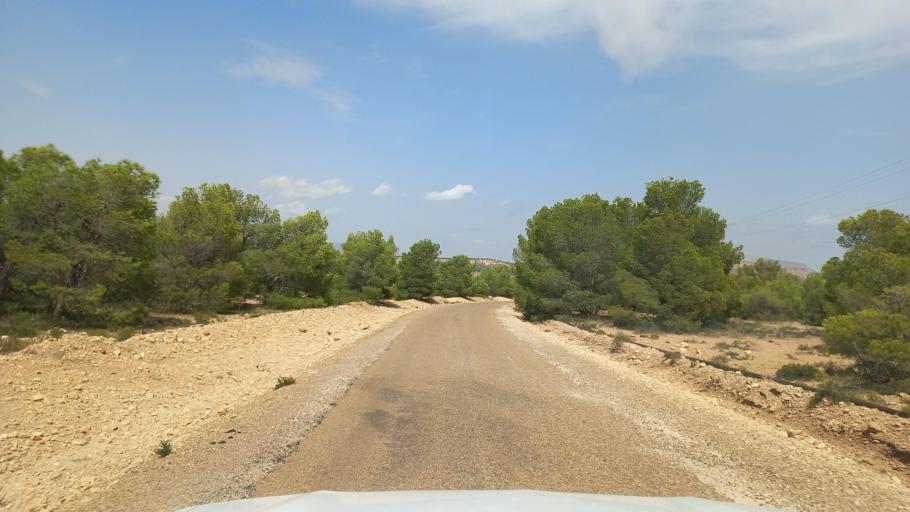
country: TN
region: Al Qasrayn
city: Sbiba
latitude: 35.3951
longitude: 8.9119
